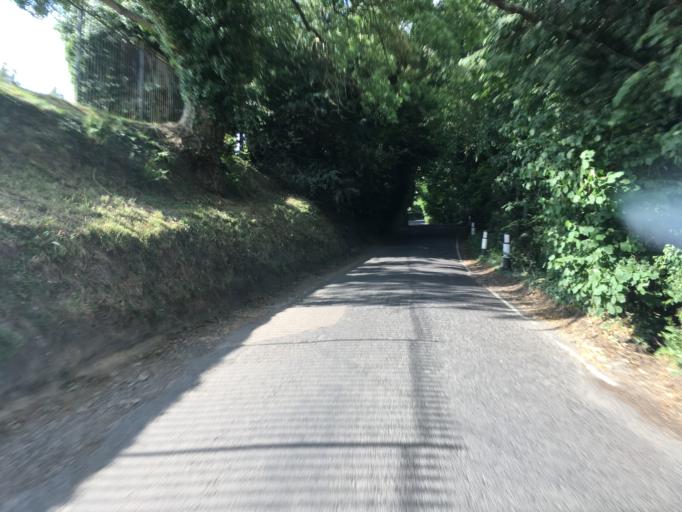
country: GB
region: England
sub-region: Kent
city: Maidstone
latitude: 51.2430
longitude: 0.5116
